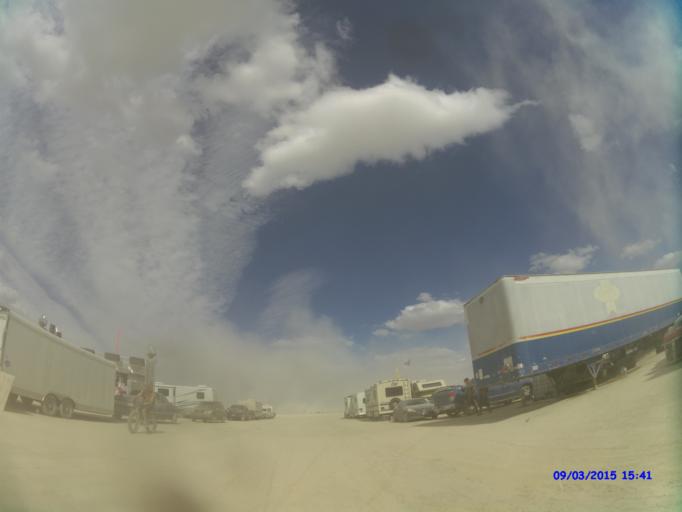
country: US
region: Nevada
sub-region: Pershing County
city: Lovelock
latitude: 40.7946
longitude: -119.2105
